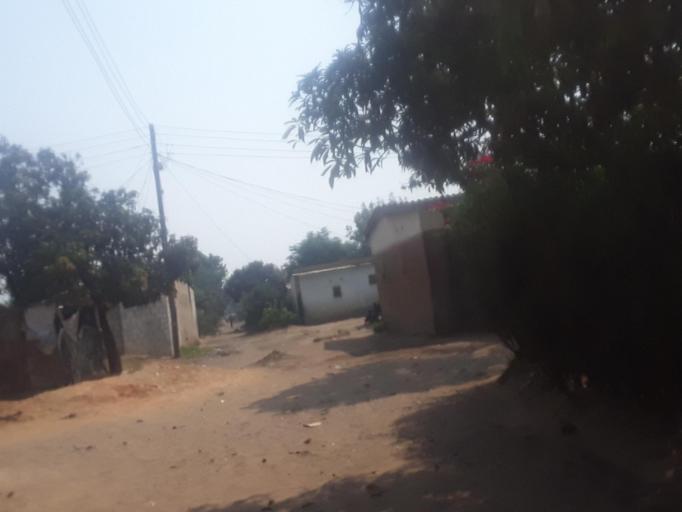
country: ZM
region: Lusaka
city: Lusaka
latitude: -15.3551
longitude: 28.2883
